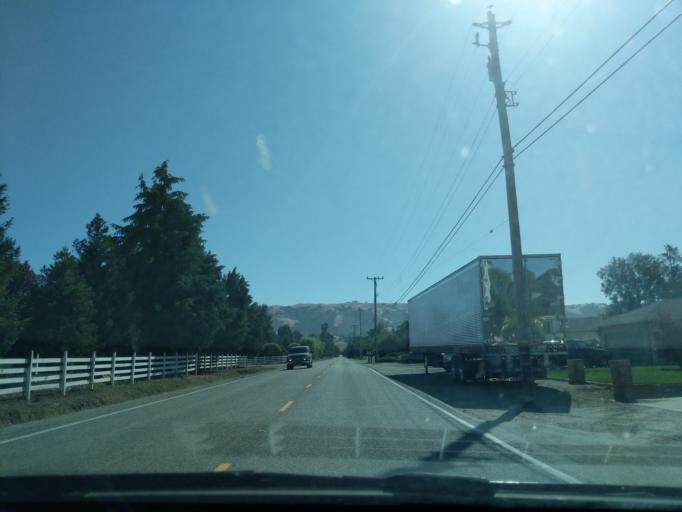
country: US
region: California
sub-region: Santa Clara County
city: Gilroy
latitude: 37.0378
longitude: -121.5375
